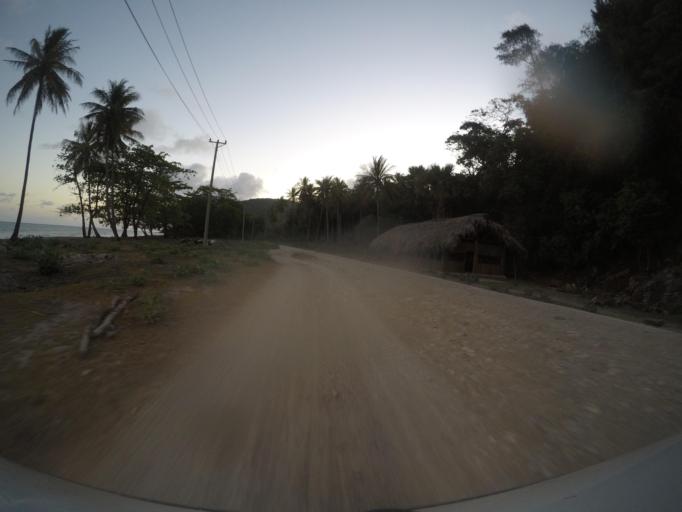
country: TL
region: Viqueque
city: Viqueque
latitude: -8.7871
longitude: 126.6328
